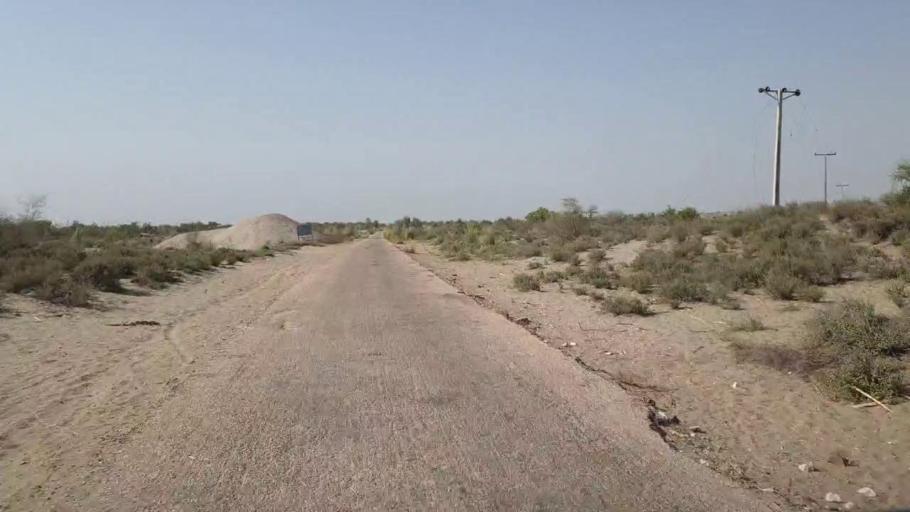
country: PK
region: Sindh
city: Jam Sahib
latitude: 26.5847
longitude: 68.9211
